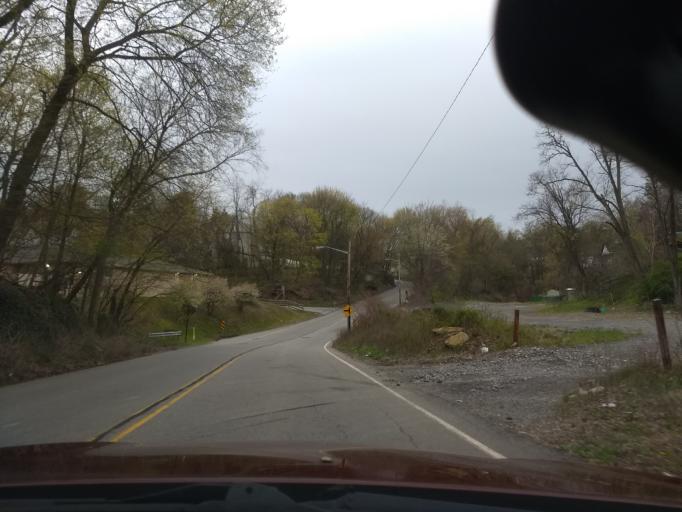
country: US
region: Pennsylvania
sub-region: Allegheny County
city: Brentwood
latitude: 40.3917
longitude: -79.9813
